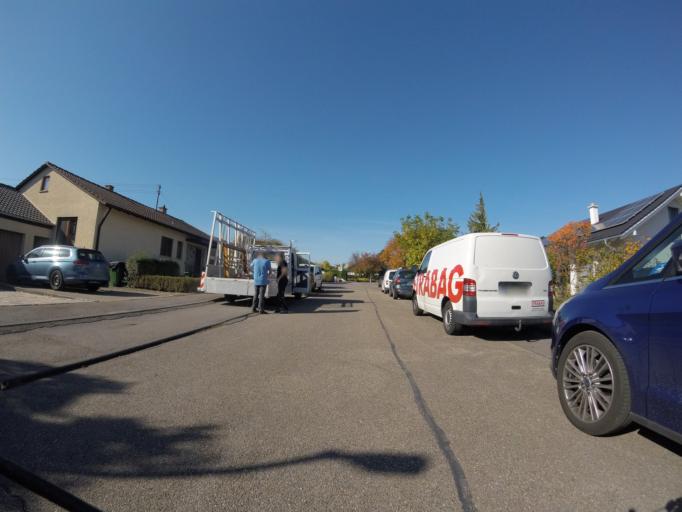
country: DE
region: Baden-Wuerttemberg
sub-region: Regierungsbezirk Stuttgart
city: Sersheim
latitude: 48.9648
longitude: 9.0179
